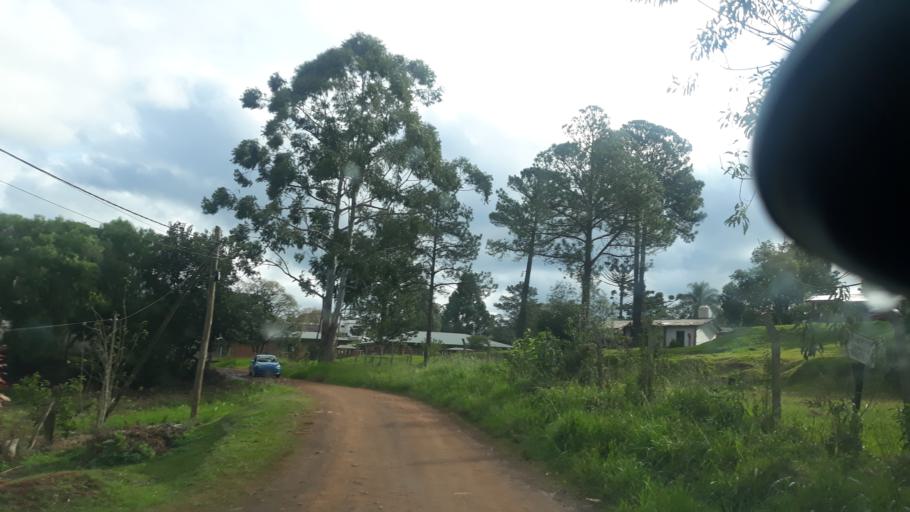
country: AR
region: Misiones
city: Bernardo de Irigoyen
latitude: -26.2625
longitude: -53.6460
